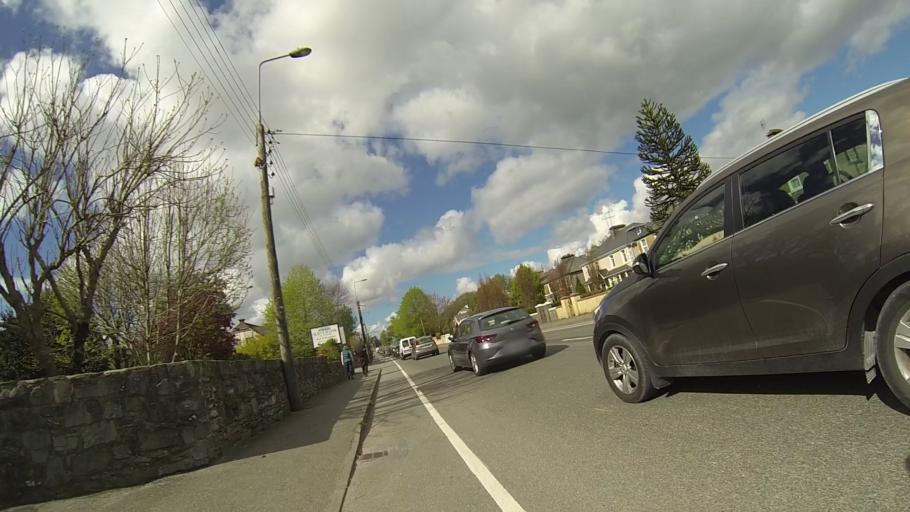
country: IE
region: Munster
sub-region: Ciarrai
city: Cill Airne
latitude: 52.0506
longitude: -9.5067
